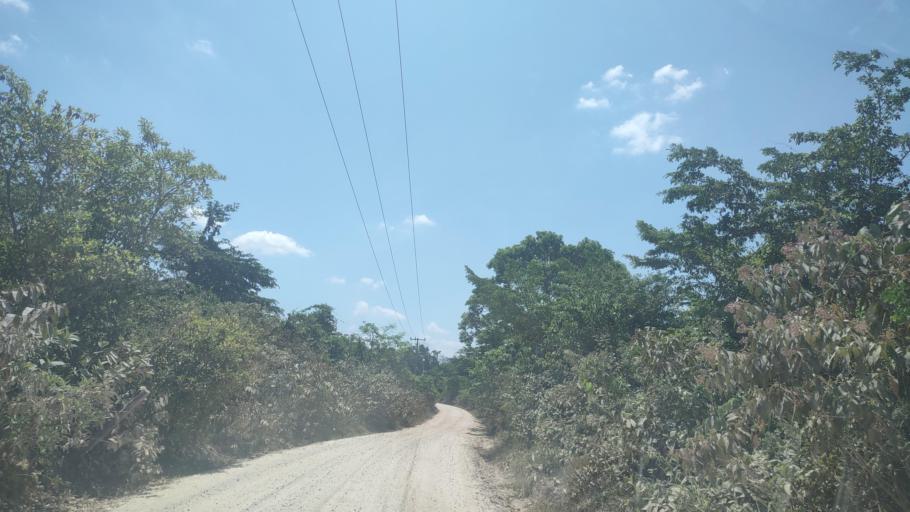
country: MX
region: Veracruz
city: Las Choapas
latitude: 17.7747
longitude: -94.1432
